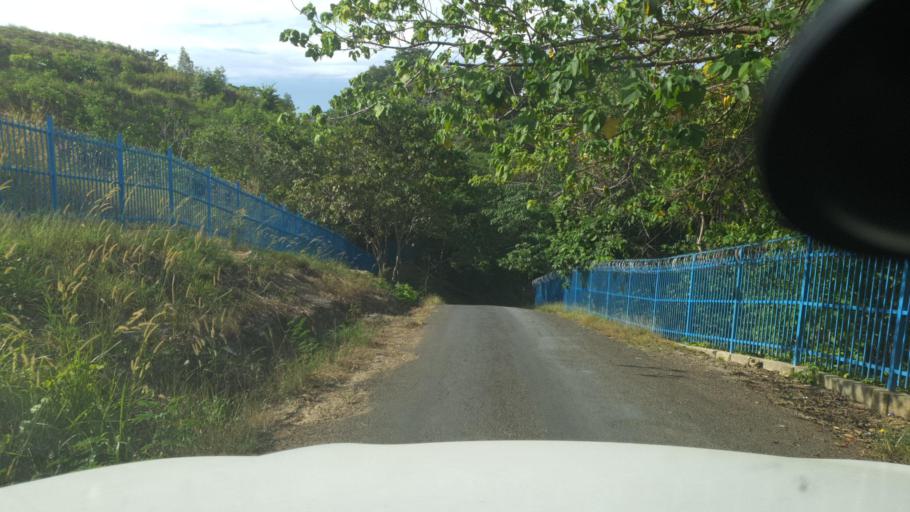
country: SB
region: Guadalcanal
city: Honiara
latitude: -9.4402
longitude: 159.9388
